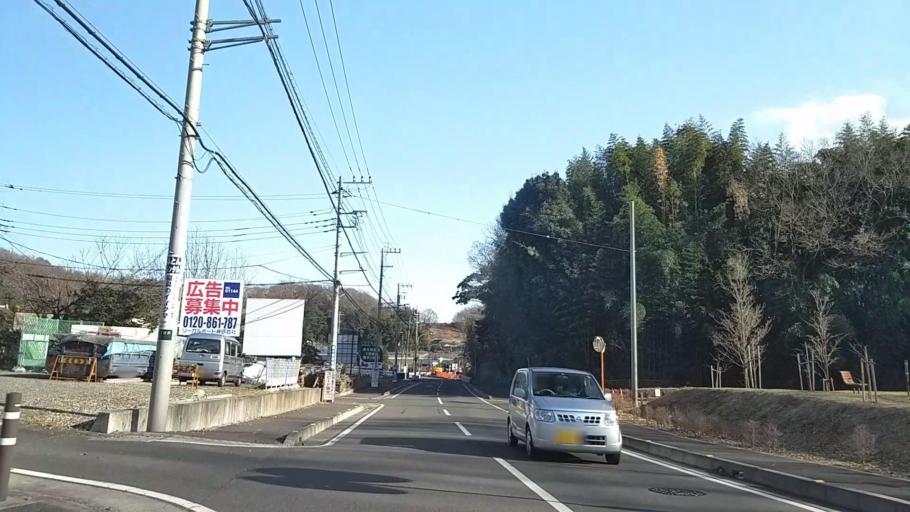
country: JP
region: Kanagawa
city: Atsugi
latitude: 35.4582
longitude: 139.3193
